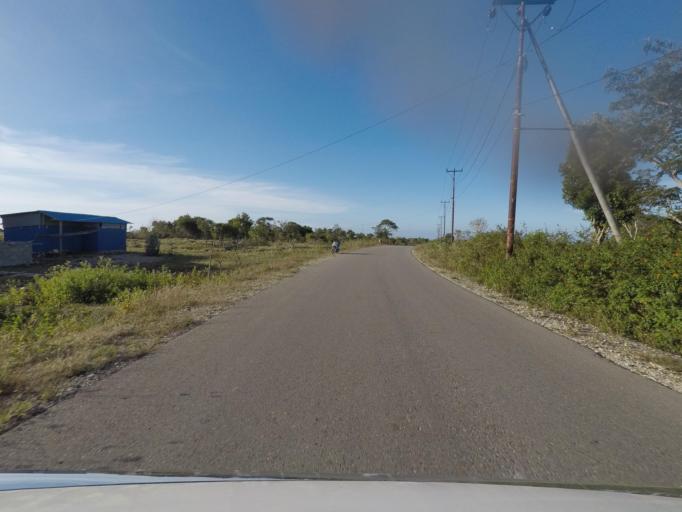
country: TL
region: Lautem
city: Lospalos
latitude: -8.3753
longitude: 127.0156
